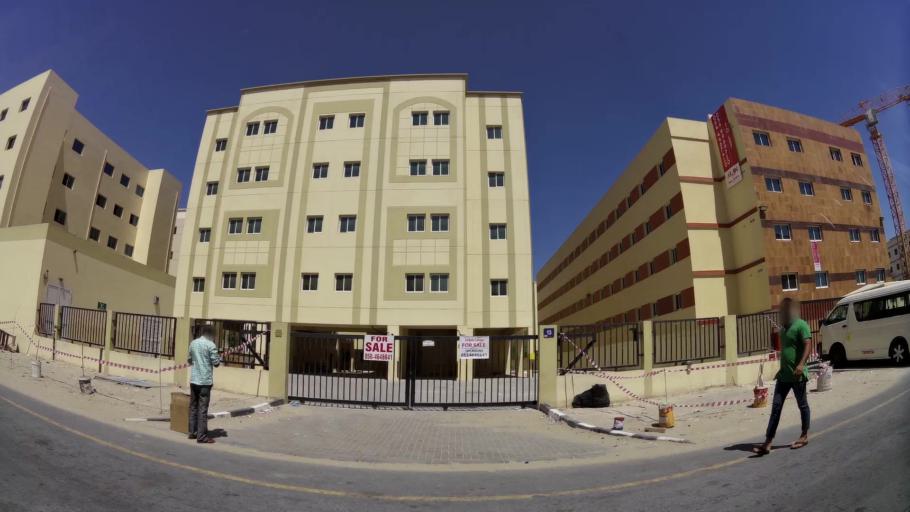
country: AE
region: Dubai
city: Dubai
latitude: 24.9766
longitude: 55.2028
